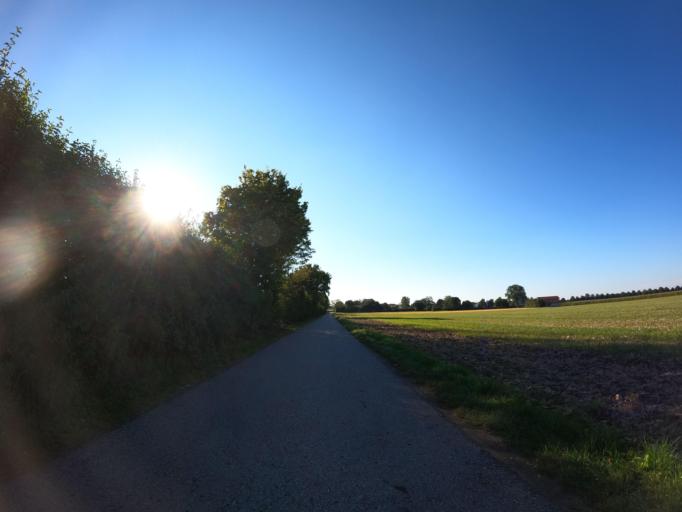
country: DE
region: Bavaria
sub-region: Upper Bavaria
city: Grasbrunn
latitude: 48.0558
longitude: 11.7822
